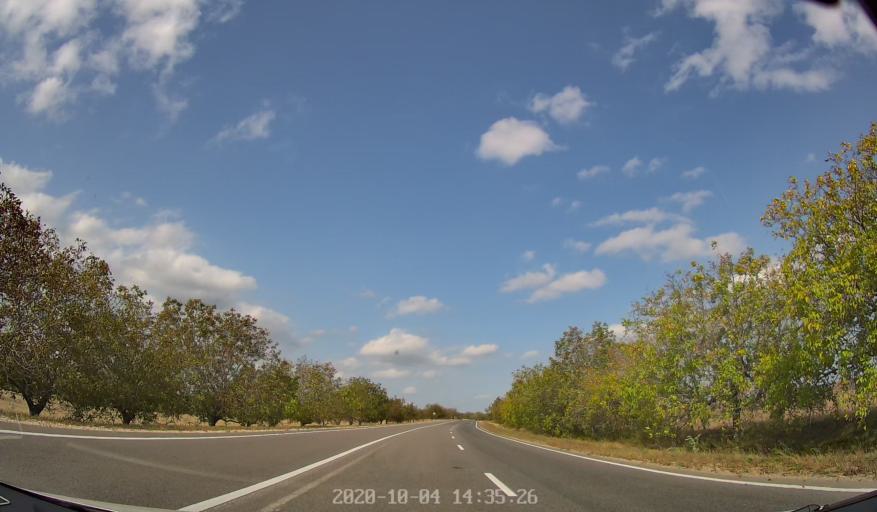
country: MD
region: Soldanesti
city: Soldanesti
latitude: 47.7162
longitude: 28.8476
